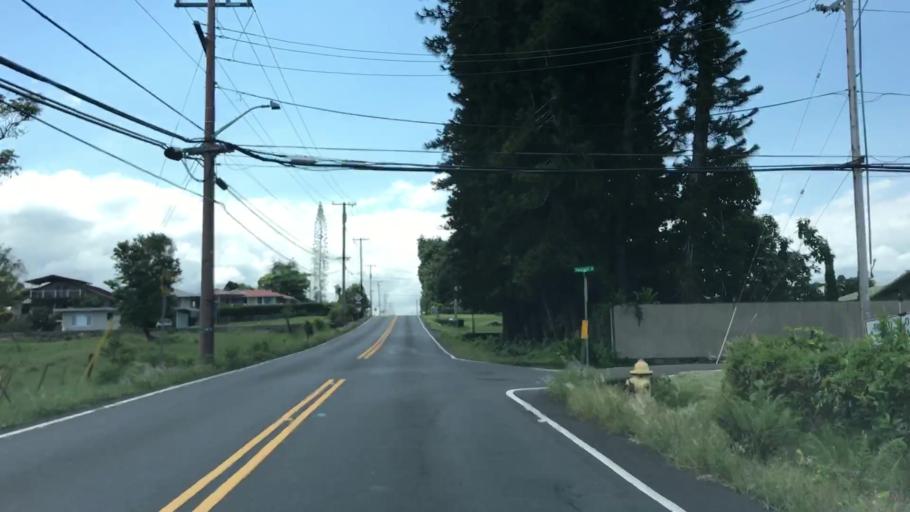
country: US
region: Hawaii
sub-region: Hawaii County
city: Hilo
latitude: 19.6738
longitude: -155.0796
